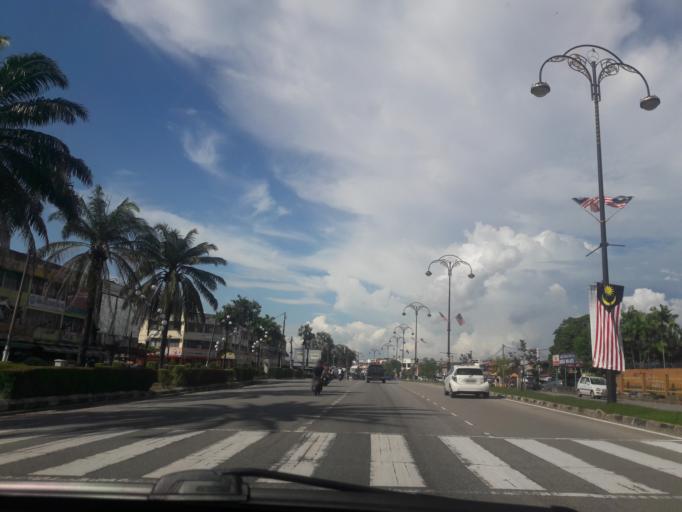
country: MY
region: Kedah
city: Sungai Petani
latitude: 5.6237
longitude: 100.4780
